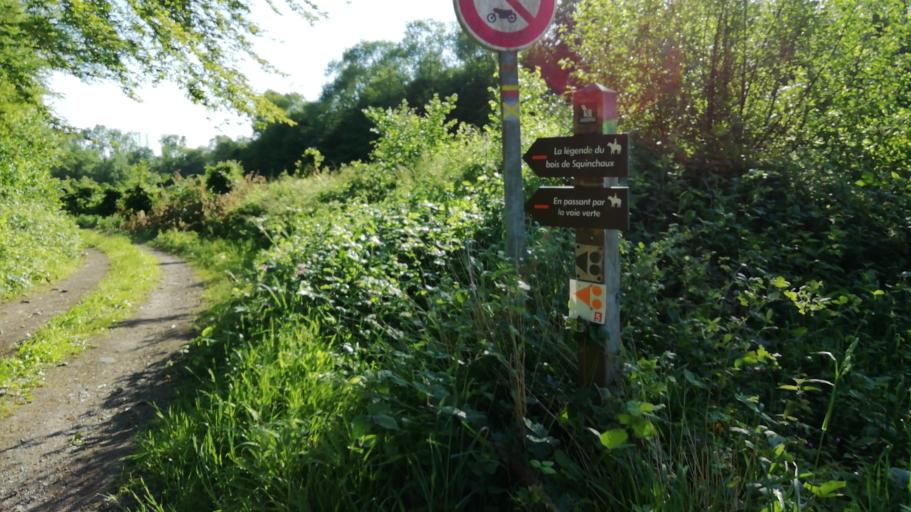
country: FR
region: Nord-Pas-de-Calais
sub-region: Departement du Nord
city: Marpent
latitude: 50.2201
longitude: 4.0818
